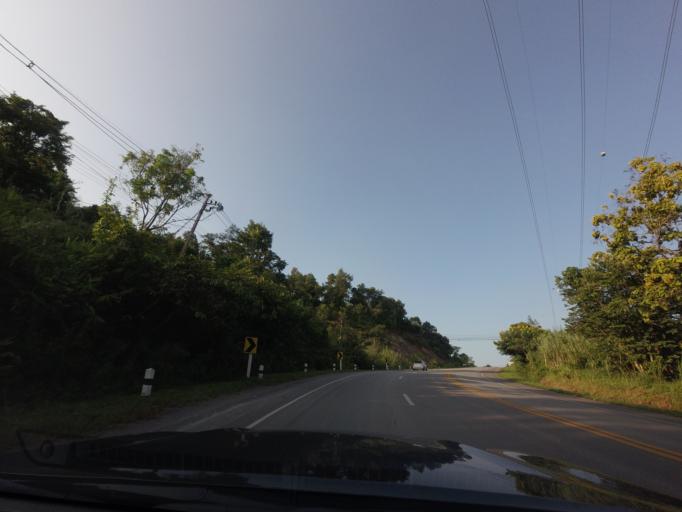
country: TH
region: Loei
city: Dan Sai
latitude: 17.2242
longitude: 101.1484
